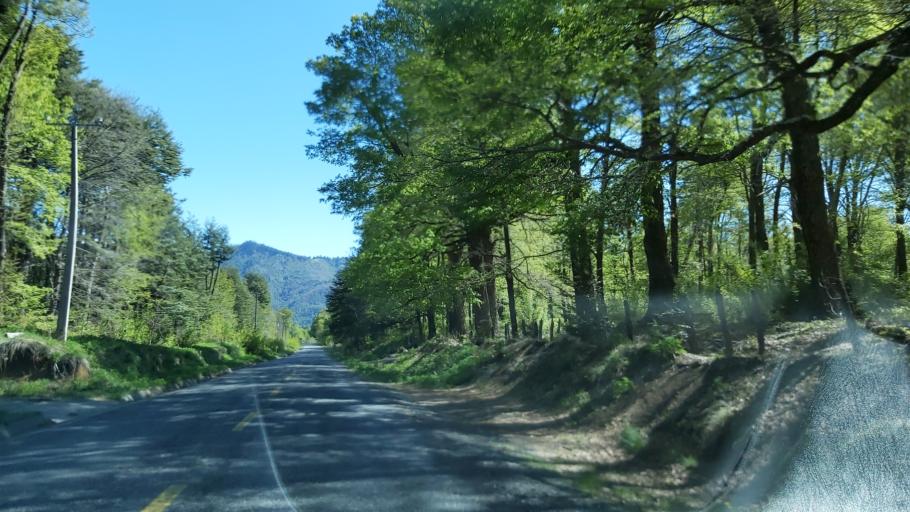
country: CL
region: Araucania
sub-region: Provincia de Cautin
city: Vilcun
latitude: -38.4703
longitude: -71.5243
